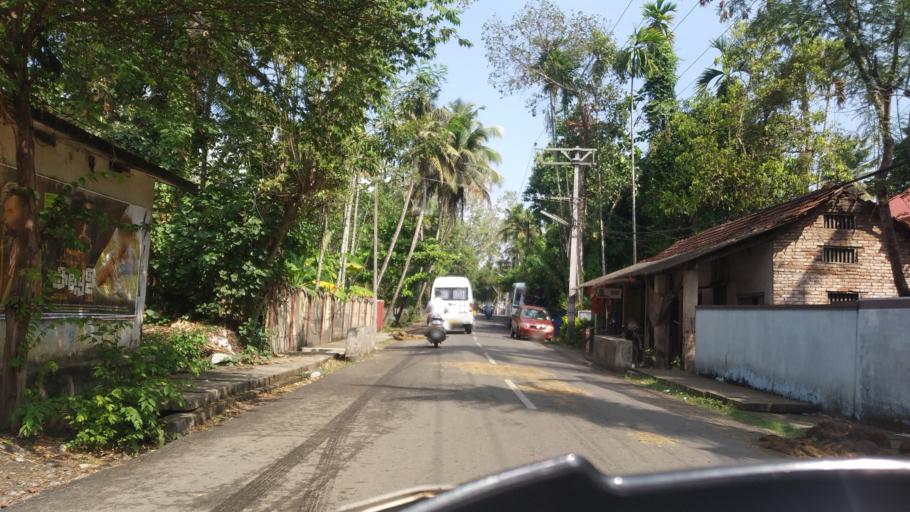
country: IN
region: Kerala
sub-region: Thrissur District
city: Kodungallur
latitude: 10.1344
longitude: 76.2209
